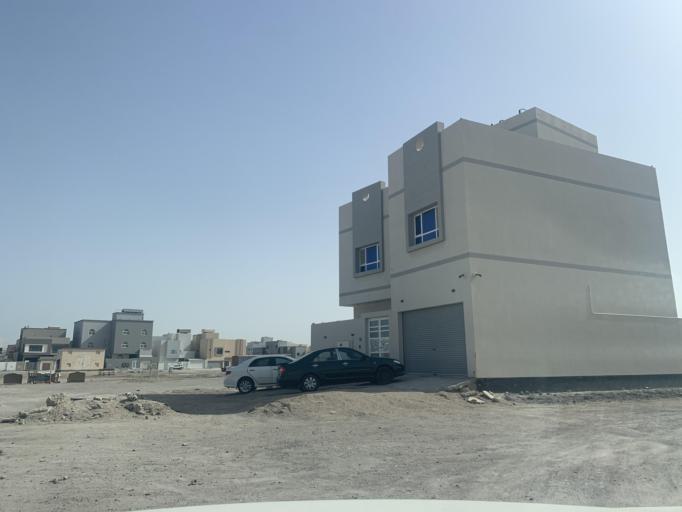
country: BH
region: Northern
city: Sitrah
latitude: 26.1670
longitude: 50.6241
